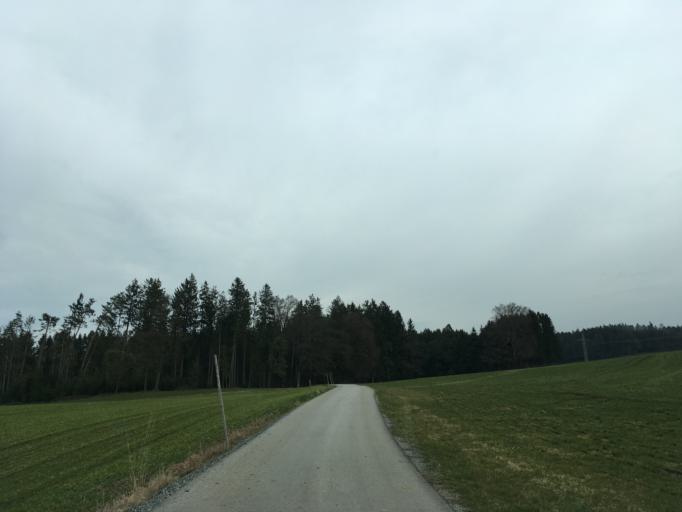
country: DE
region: Bavaria
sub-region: Upper Bavaria
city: Schnaitsee
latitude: 48.0579
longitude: 12.3743
